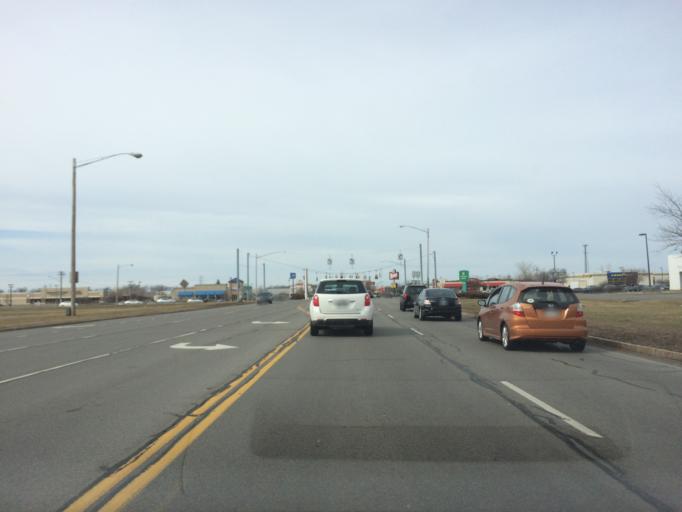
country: US
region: New York
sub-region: Monroe County
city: Rochester
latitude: 43.0857
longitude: -77.6296
